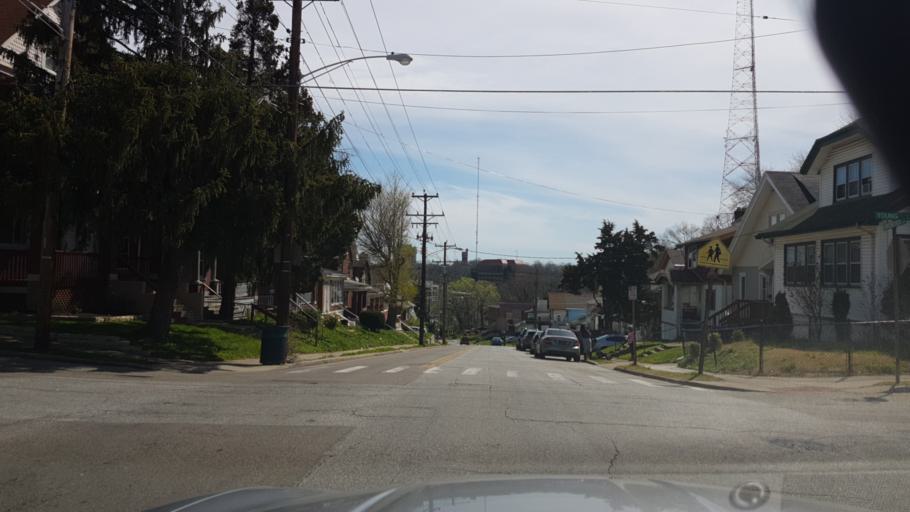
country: US
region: Kentucky
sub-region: Campbell County
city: Newport
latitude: 39.1179
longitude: -84.5064
